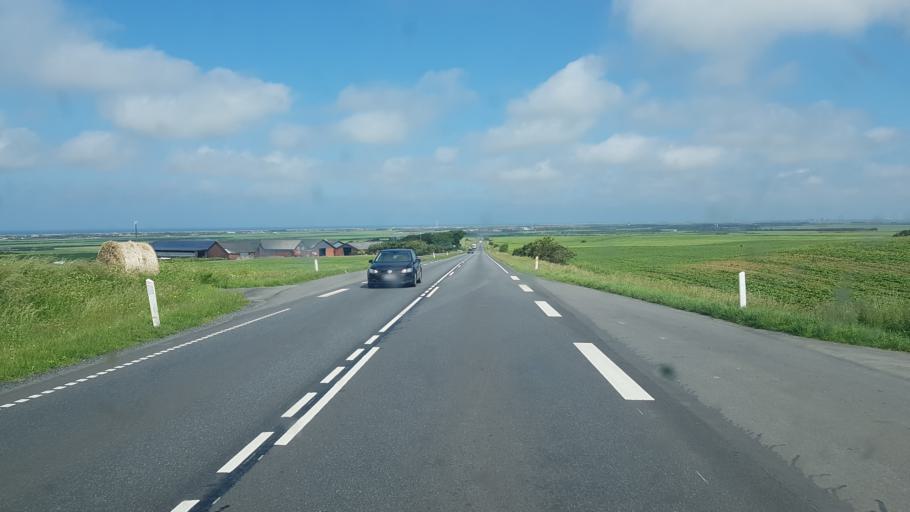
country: DK
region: Central Jutland
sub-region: Lemvig Kommune
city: Harboore
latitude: 56.5839
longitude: 8.1980
